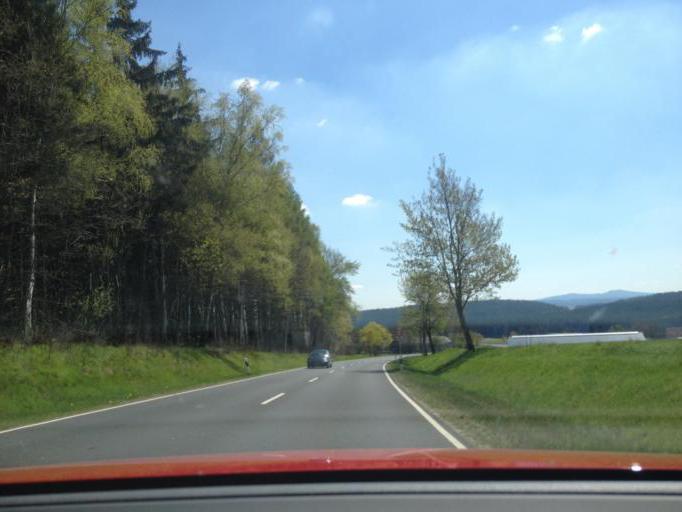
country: DE
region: Bavaria
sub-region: Upper Franconia
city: Kirchenlamitz
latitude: 50.1431
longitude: 11.9679
